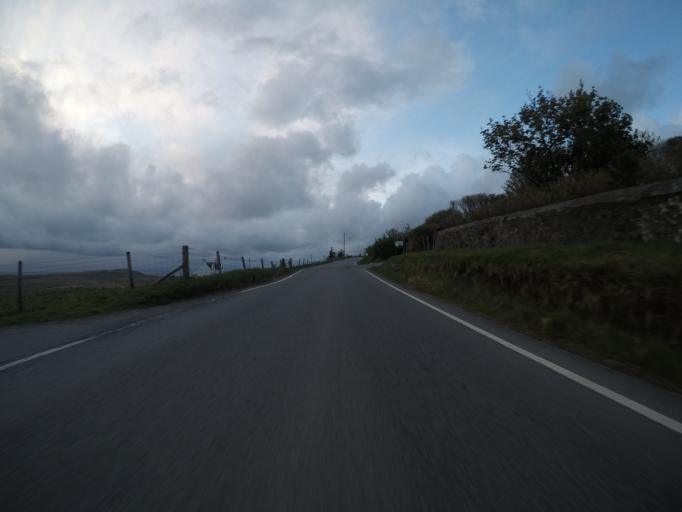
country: GB
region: Scotland
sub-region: Highland
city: Portree
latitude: 57.6296
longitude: -6.3783
